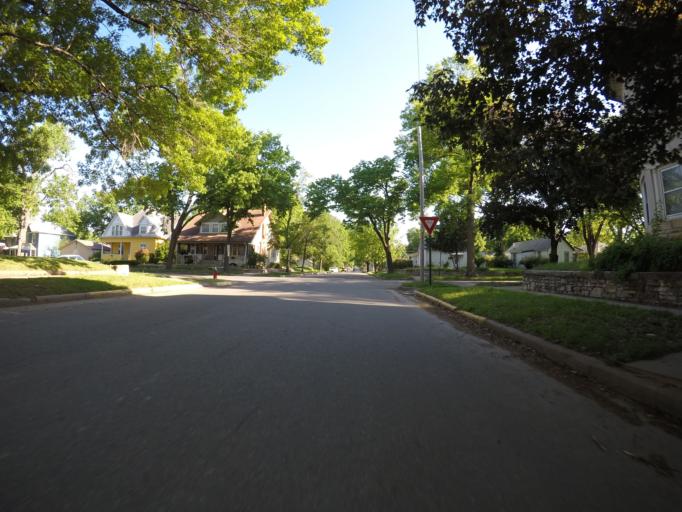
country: US
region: Kansas
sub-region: Riley County
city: Manhattan
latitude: 39.1819
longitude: -96.5717
